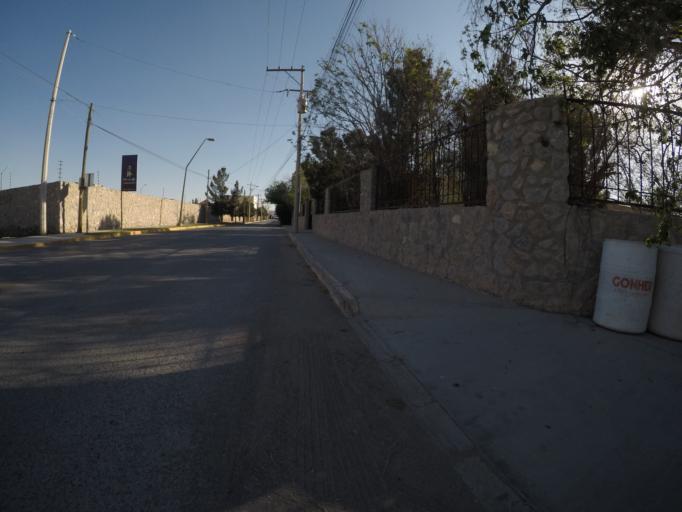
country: MX
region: Chihuahua
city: Ciudad Juarez
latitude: 31.7037
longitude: -106.3980
